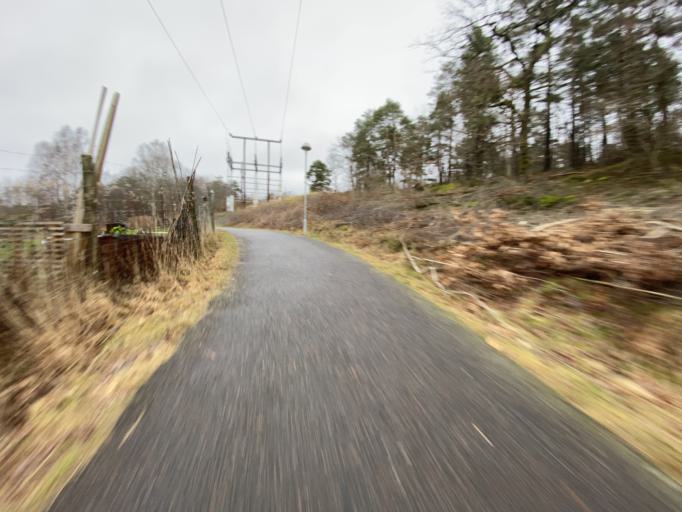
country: SE
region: Vaestra Goetaland
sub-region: Molndal
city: Moelndal
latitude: 57.7090
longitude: 12.0398
